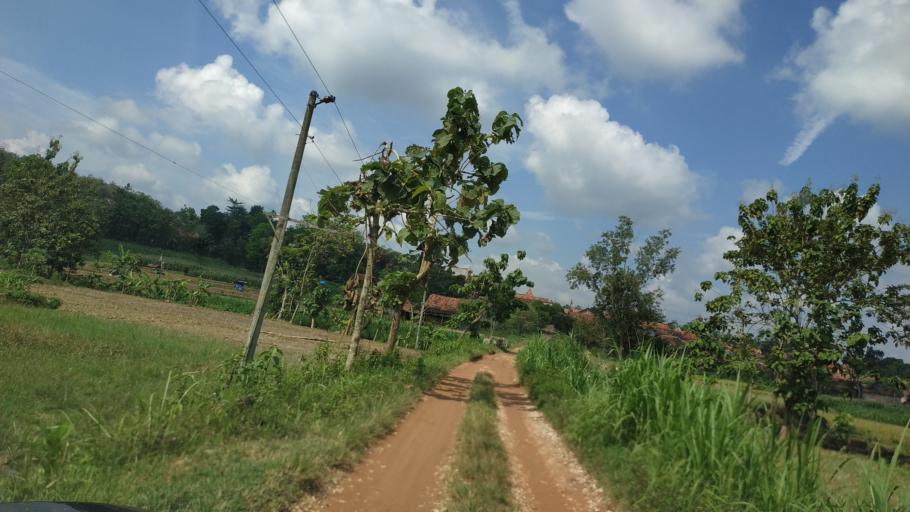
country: ID
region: Central Java
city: Guyangan
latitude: -7.0058
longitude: 111.1044
